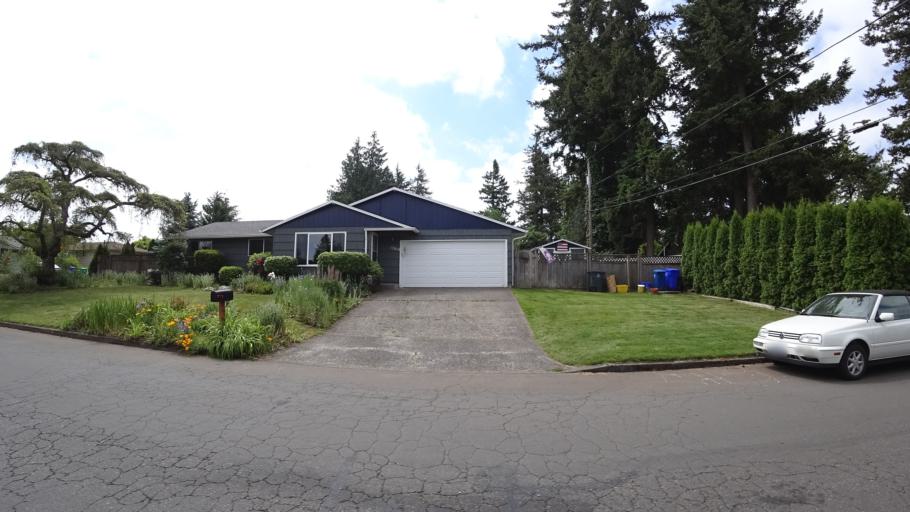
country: US
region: Oregon
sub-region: Multnomah County
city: Gresham
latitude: 45.4981
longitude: -122.4819
